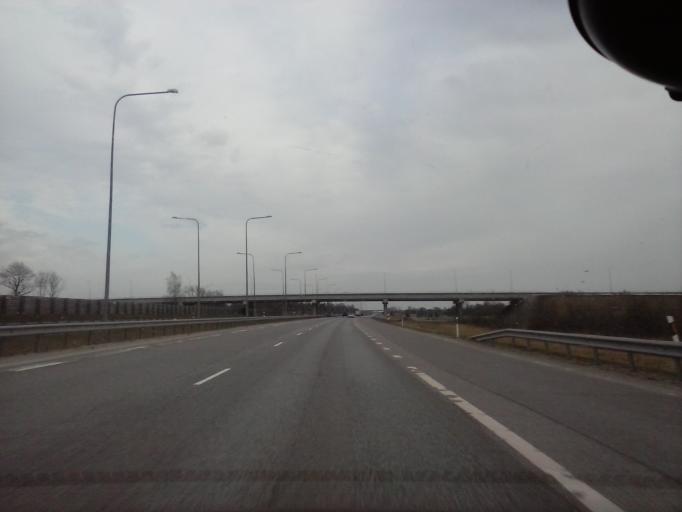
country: EE
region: Harju
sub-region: Rae vald
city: Vaida
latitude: 59.2917
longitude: 24.9643
